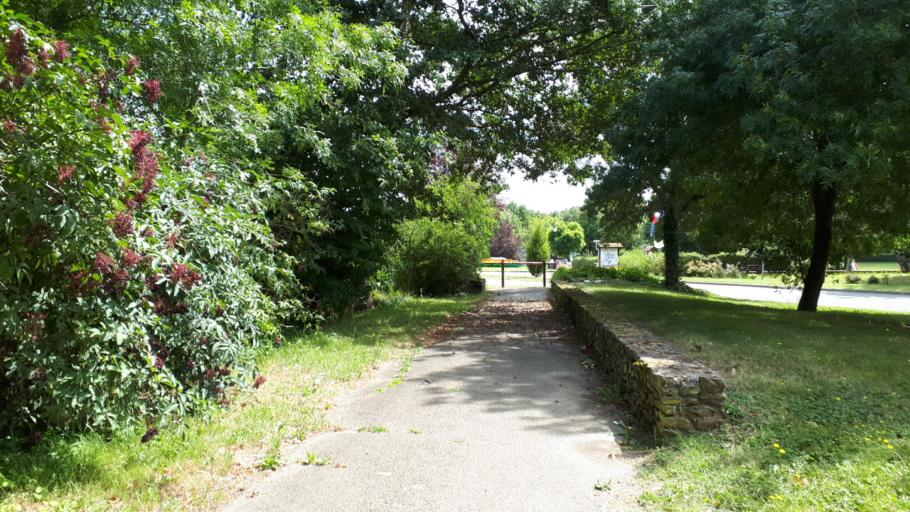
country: FR
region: Pays de la Loire
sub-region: Departement de Maine-et-Loire
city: Rochefort-sur-Loire
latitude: 47.3283
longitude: -0.6723
